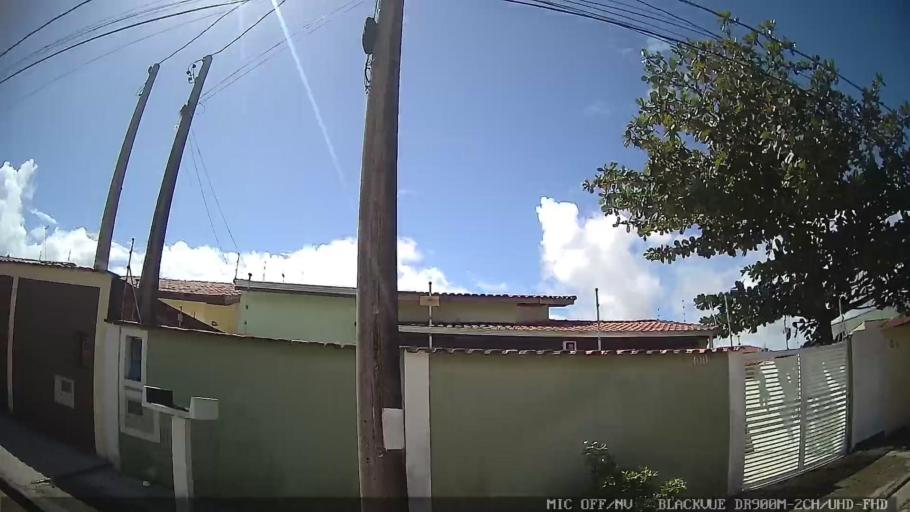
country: BR
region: Sao Paulo
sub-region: Itanhaem
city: Itanhaem
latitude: -24.2297
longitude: -46.8678
